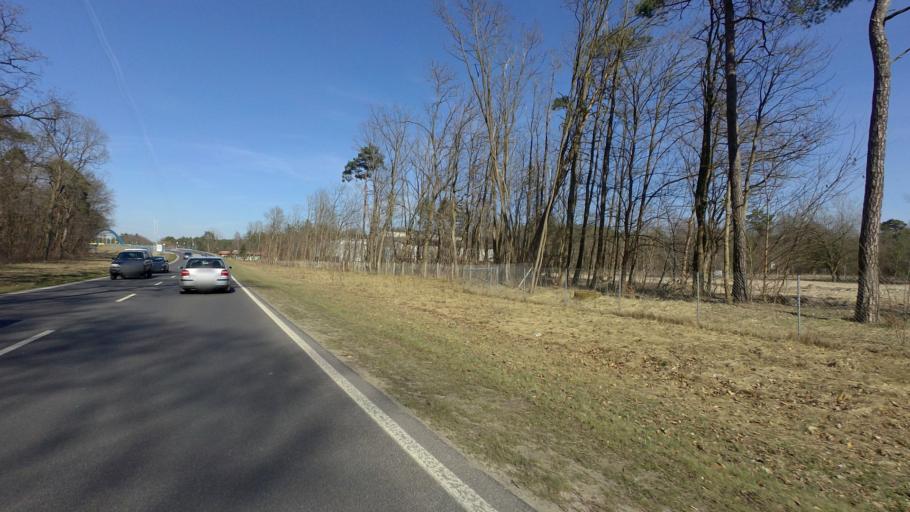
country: DE
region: Brandenburg
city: Eberswalde
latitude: 52.8538
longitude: 13.8273
